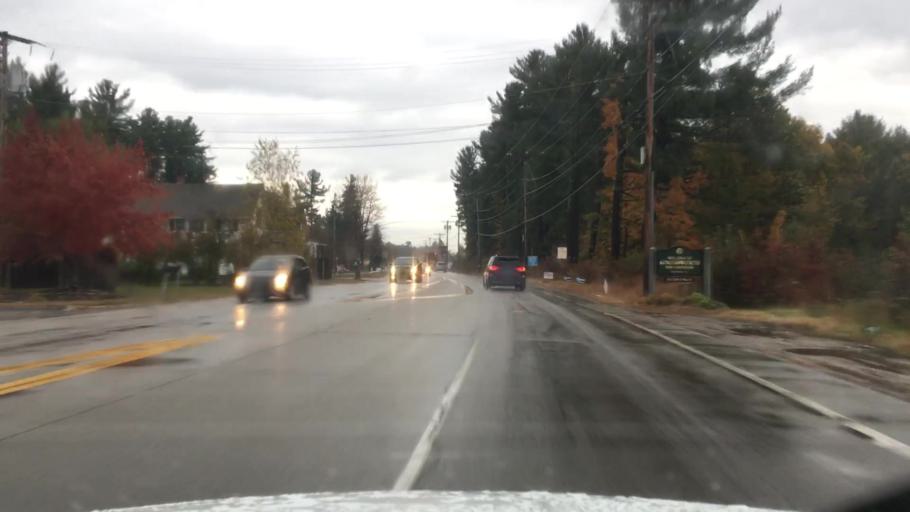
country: US
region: New Hampshire
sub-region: Strafford County
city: Dover
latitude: 43.2324
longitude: -70.8971
